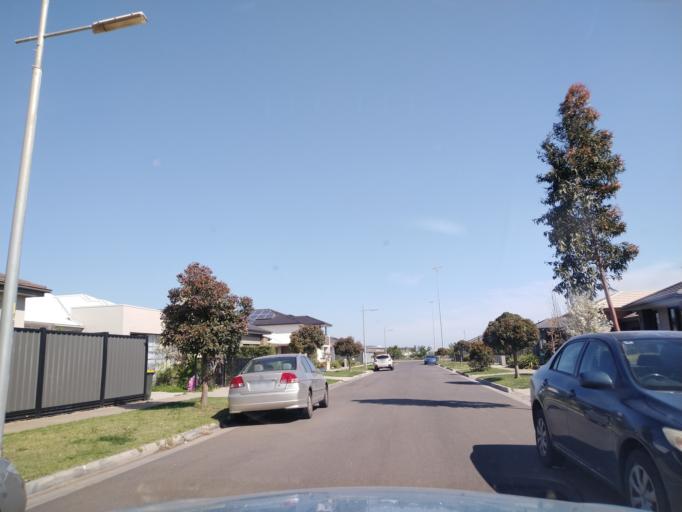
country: AU
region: Victoria
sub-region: Wyndham
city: Williams Landing
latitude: -37.8388
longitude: 144.7360
